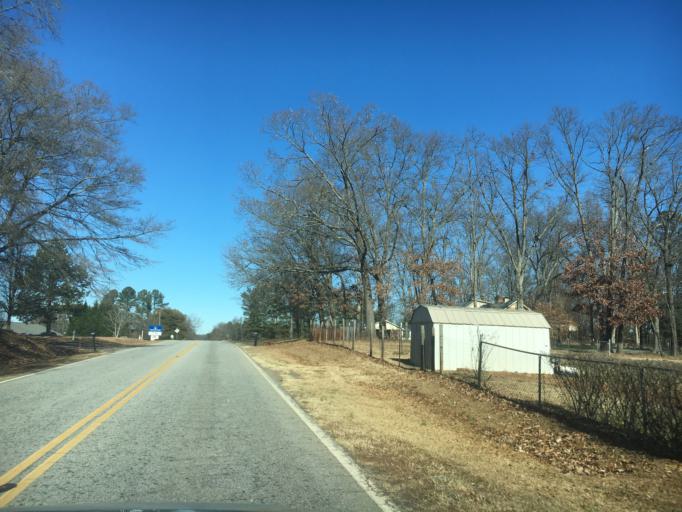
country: US
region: South Carolina
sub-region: Spartanburg County
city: Duncan
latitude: 34.9119
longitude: -82.1331
